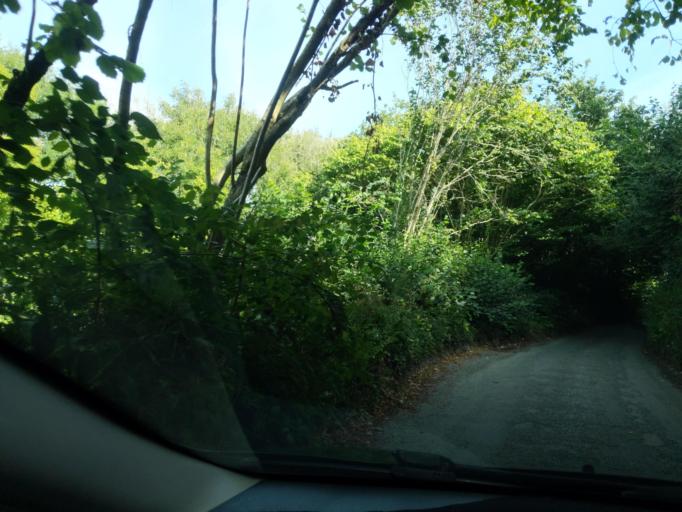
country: GB
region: England
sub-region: Cornwall
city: Torpoint
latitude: 50.3572
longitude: -4.2255
